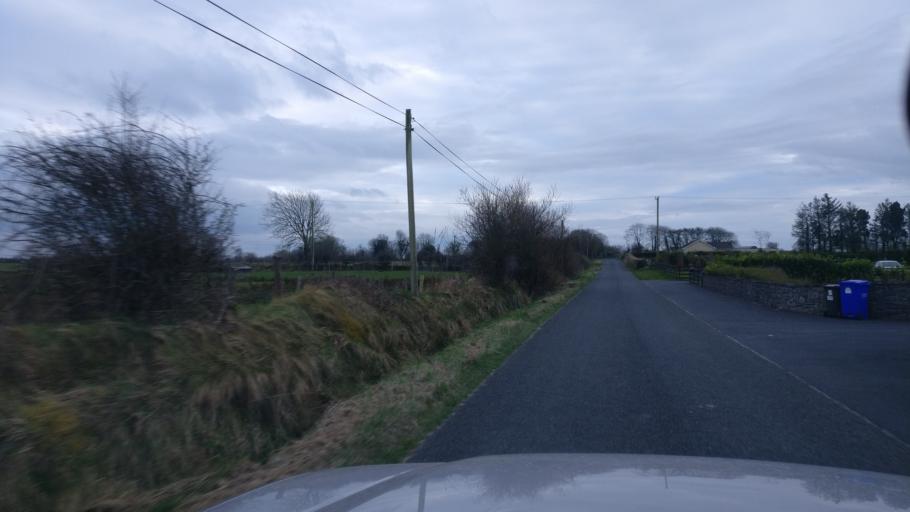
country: IE
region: Connaught
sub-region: County Galway
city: Loughrea
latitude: 53.2574
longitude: -8.5084
